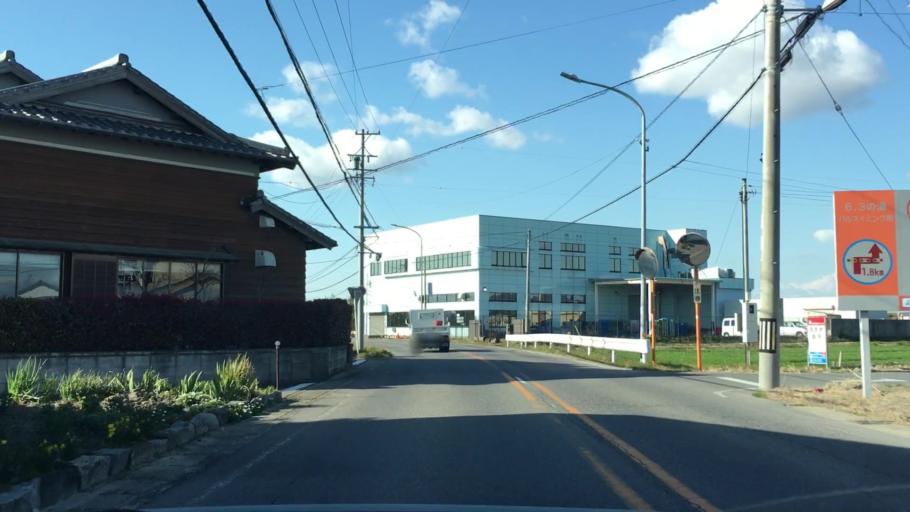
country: JP
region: Aichi
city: Nishio
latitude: 34.8439
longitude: 137.0478
